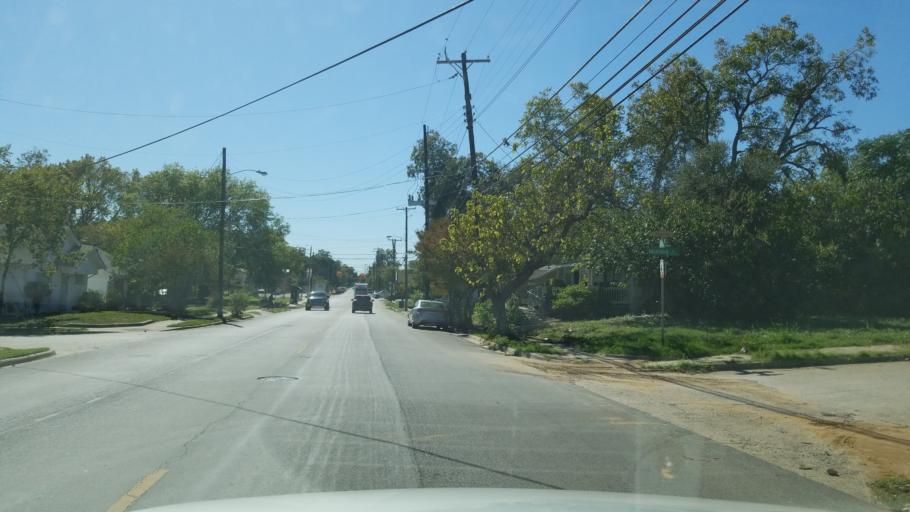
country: US
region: Texas
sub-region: Dallas County
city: Dallas
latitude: 32.7726
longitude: -96.7448
